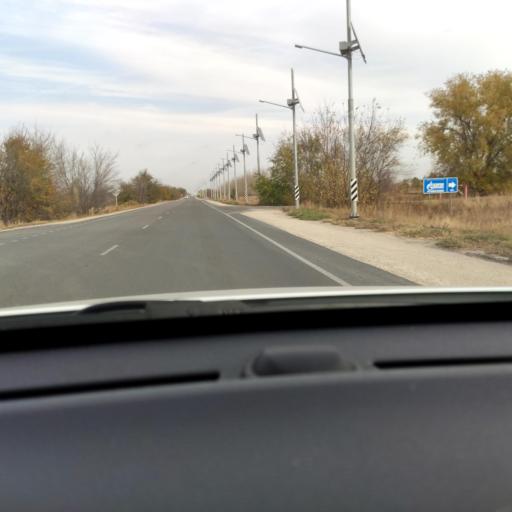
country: RU
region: Voronezj
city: Novaya Usman'
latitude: 51.6592
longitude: 39.4389
